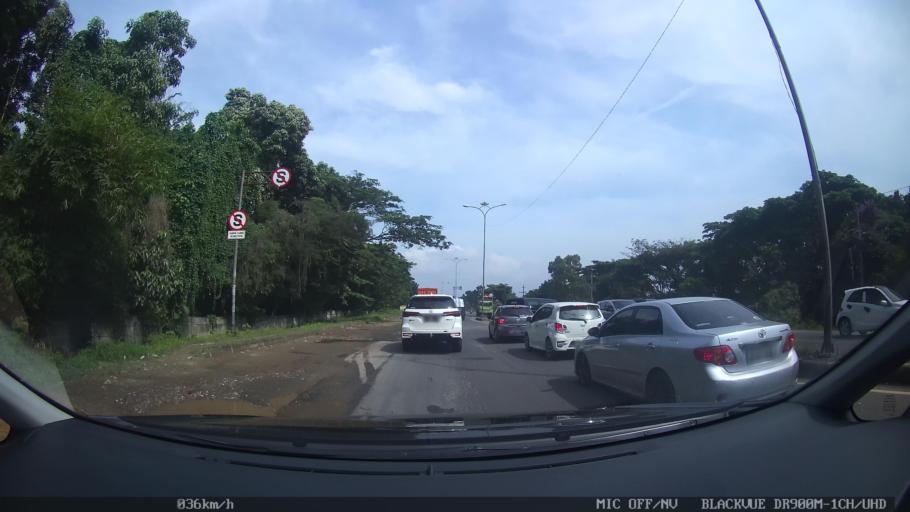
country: ID
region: Lampung
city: Kedaton
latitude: -5.3794
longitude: 105.2833
